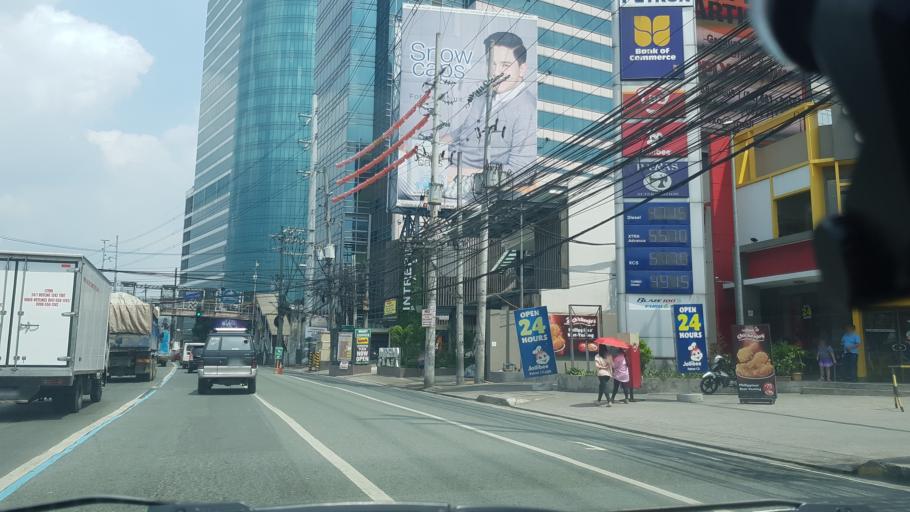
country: PH
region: Metro Manila
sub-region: Marikina
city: Calumpang
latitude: 14.6062
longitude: 121.0790
